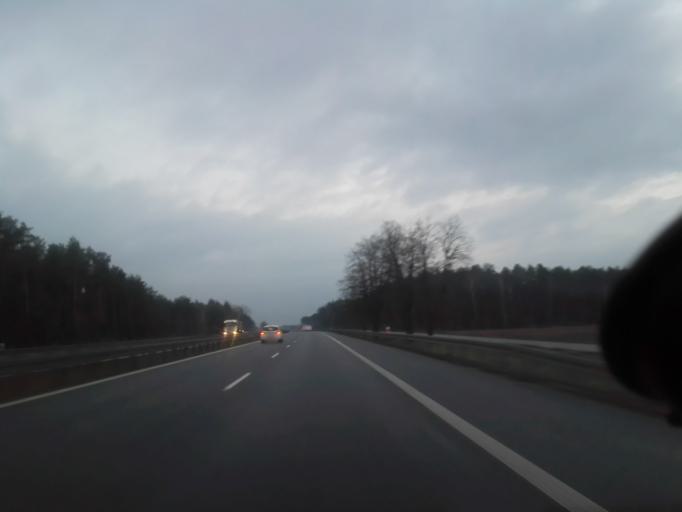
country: PL
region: Masovian Voivodeship
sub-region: Powiat wolominski
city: Dabrowka
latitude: 52.4977
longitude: 21.3750
